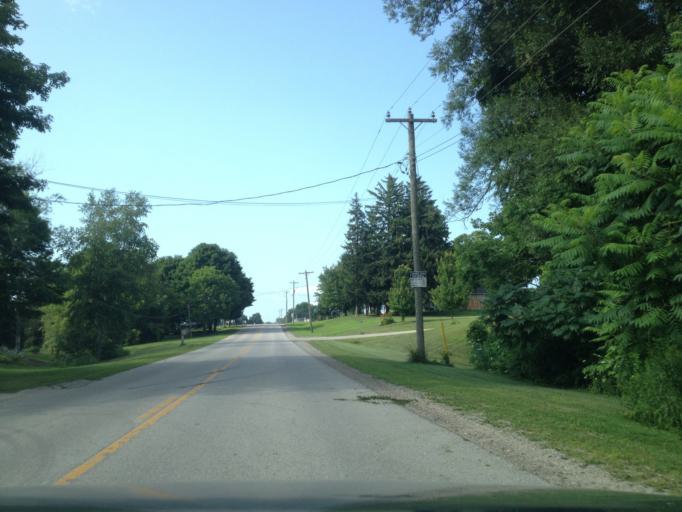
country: CA
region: Ontario
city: Aylmer
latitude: 42.7140
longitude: -80.8590
